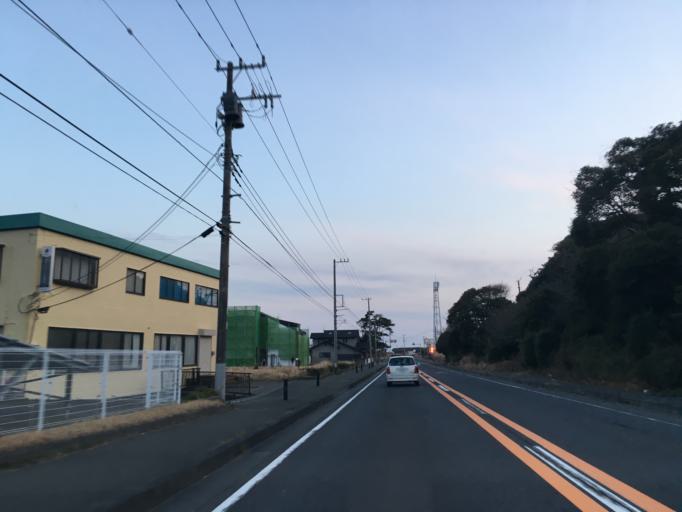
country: JP
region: Ibaraki
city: Kitaibaraki
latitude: 36.7621
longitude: 140.7371
